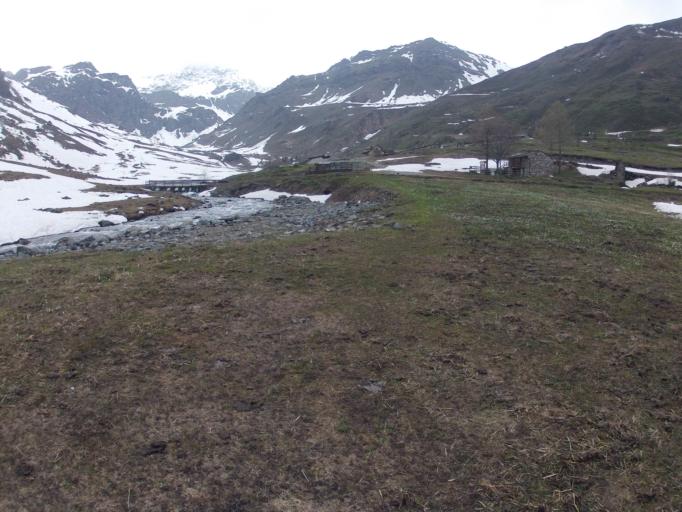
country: IT
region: Piedmont
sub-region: Provincia di Cuneo
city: Crissolo
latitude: 44.6994
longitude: 7.1203
